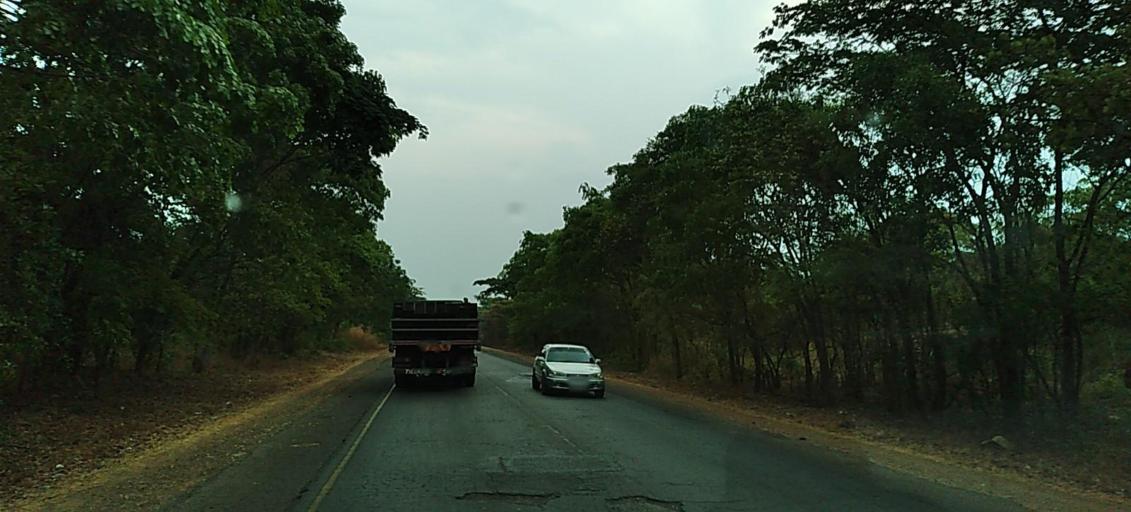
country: ZM
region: Copperbelt
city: Luanshya
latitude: -13.0628
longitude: 28.4557
